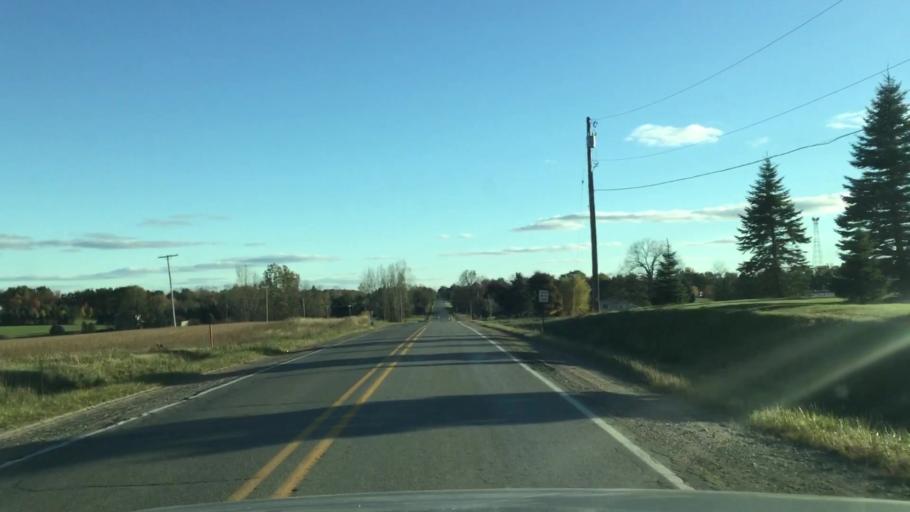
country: US
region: Michigan
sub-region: Lapeer County
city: Imlay City
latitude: 42.9583
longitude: -83.1456
